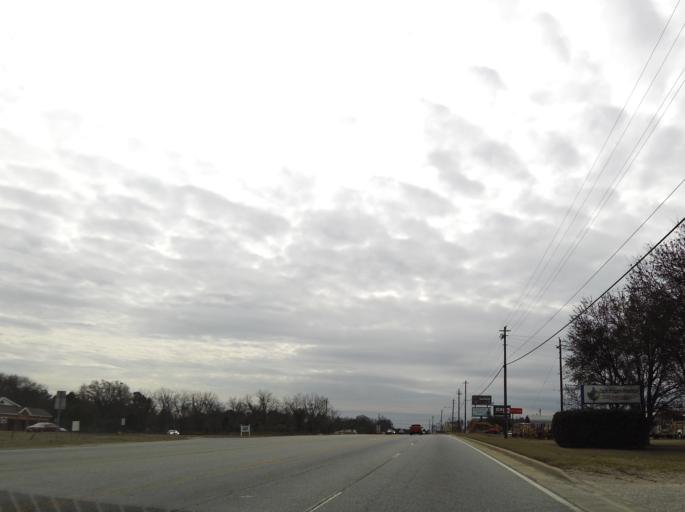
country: US
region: Georgia
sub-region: Peach County
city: Byron
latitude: 32.6477
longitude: -83.7607
